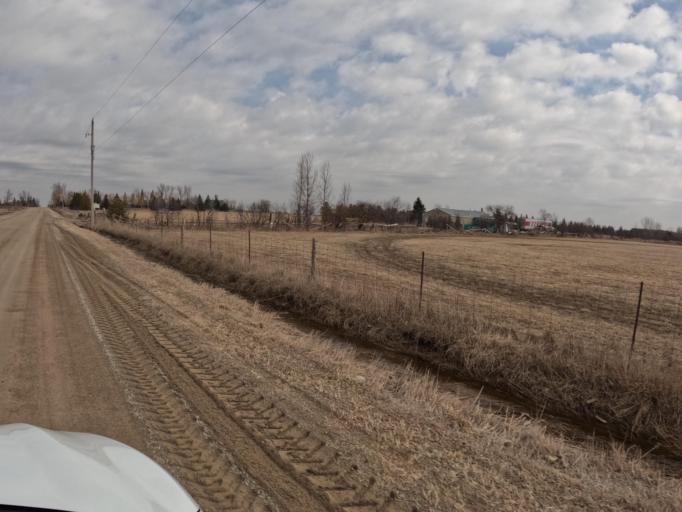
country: CA
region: Ontario
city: Orangeville
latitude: 43.9049
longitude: -80.2143
